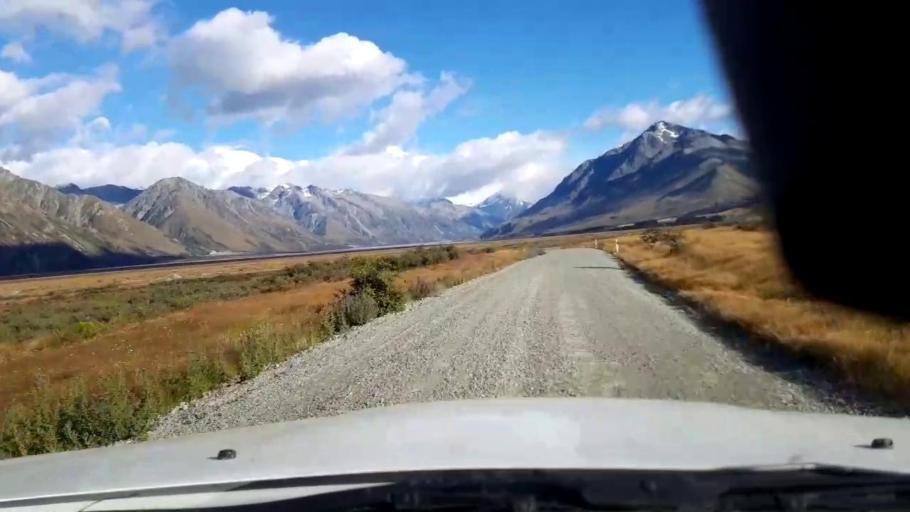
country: NZ
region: Canterbury
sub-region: Timaru District
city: Pleasant Point
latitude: -43.7416
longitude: 170.5707
